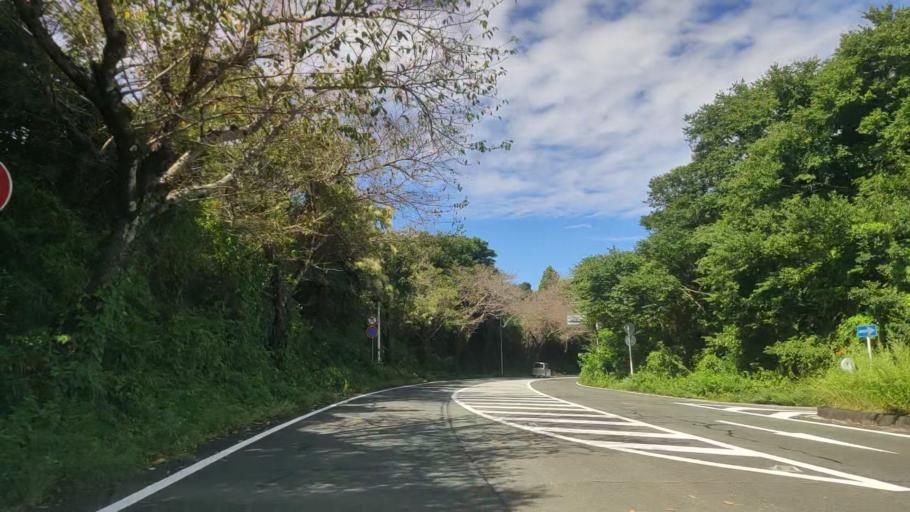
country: JP
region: Shizuoka
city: Kosai-shi
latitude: 34.7337
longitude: 137.5962
